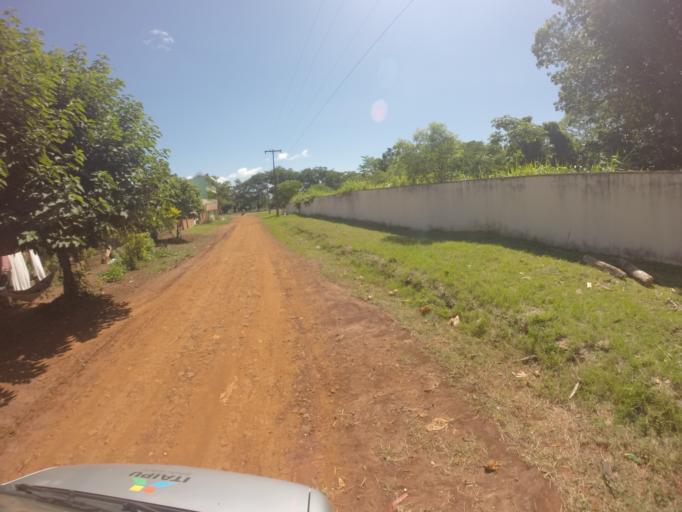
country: PY
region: Alto Parana
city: Ciudad del Este
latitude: -25.4378
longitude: -54.6366
